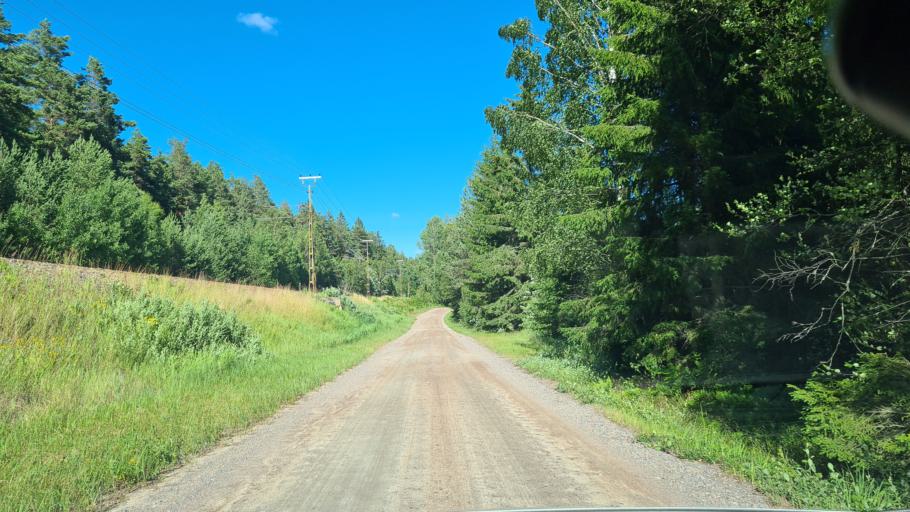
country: SE
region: OEstergoetland
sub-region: Norrkopings Kommun
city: Krokek
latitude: 58.7006
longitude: 16.4297
